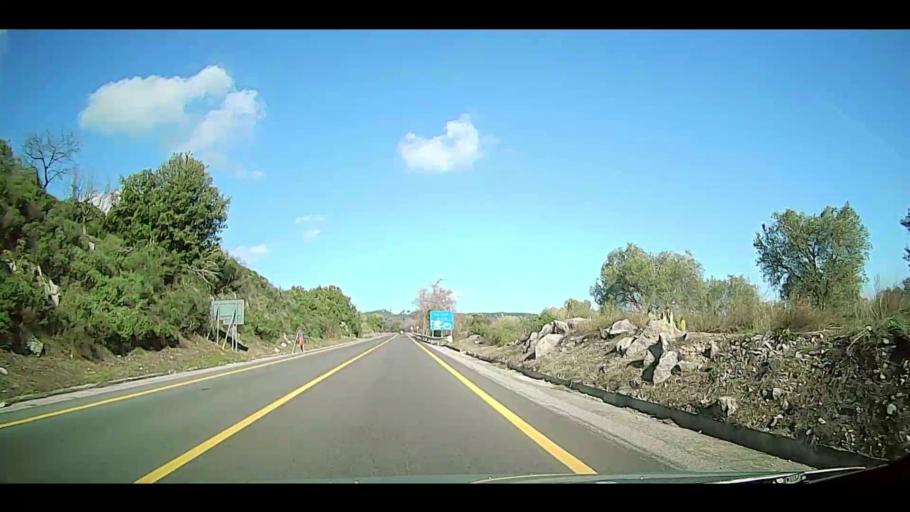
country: IT
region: Calabria
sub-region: Provincia di Crotone
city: Caccuri
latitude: 39.2285
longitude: 16.7950
